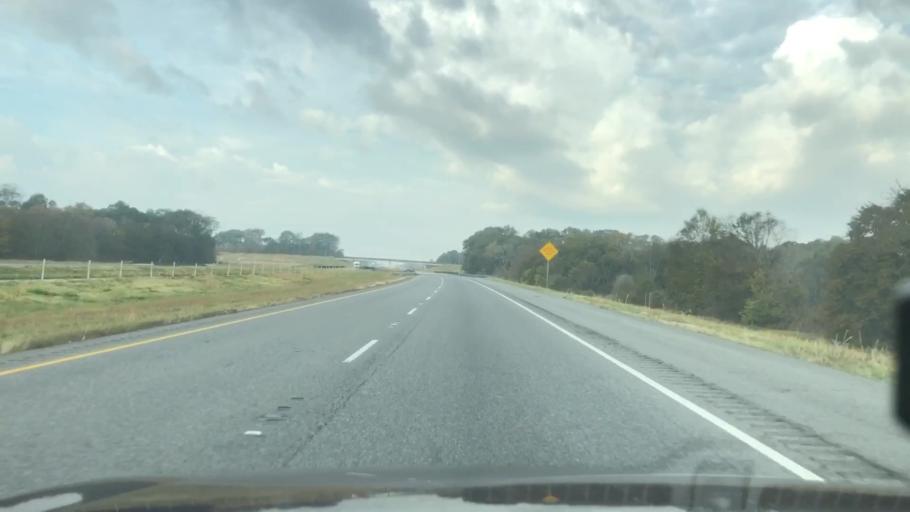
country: US
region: Louisiana
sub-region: Madison Parish
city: Tallulah
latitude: 32.4190
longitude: -91.2946
